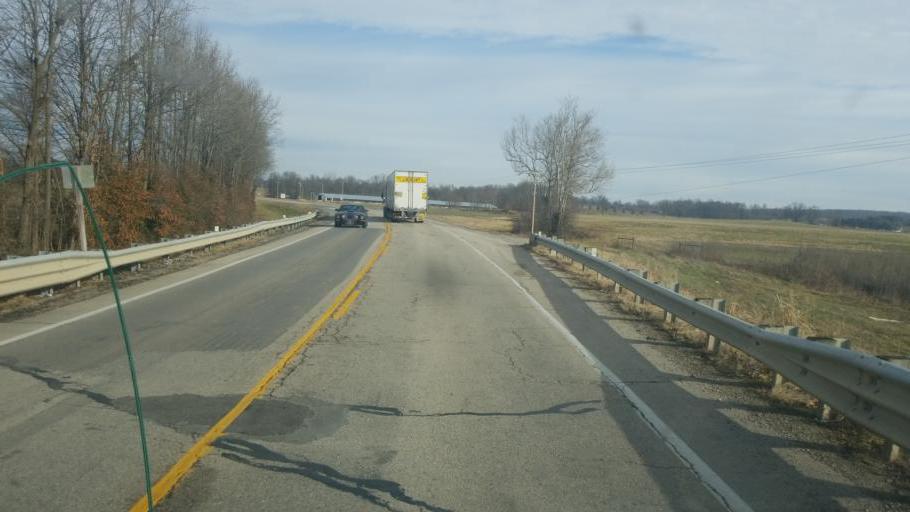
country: US
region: Missouri
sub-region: Stoddard County
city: Bloomfield
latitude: 36.9526
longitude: -89.9071
